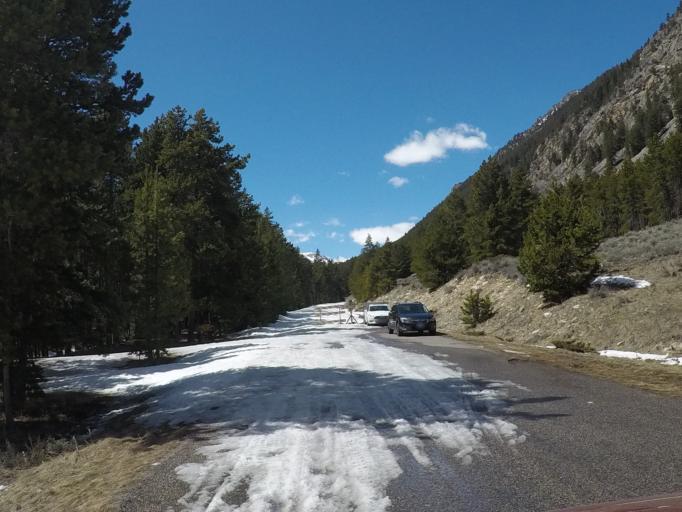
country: US
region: Montana
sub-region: Carbon County
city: Red Lodge
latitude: 45.0812
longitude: -109.3846
